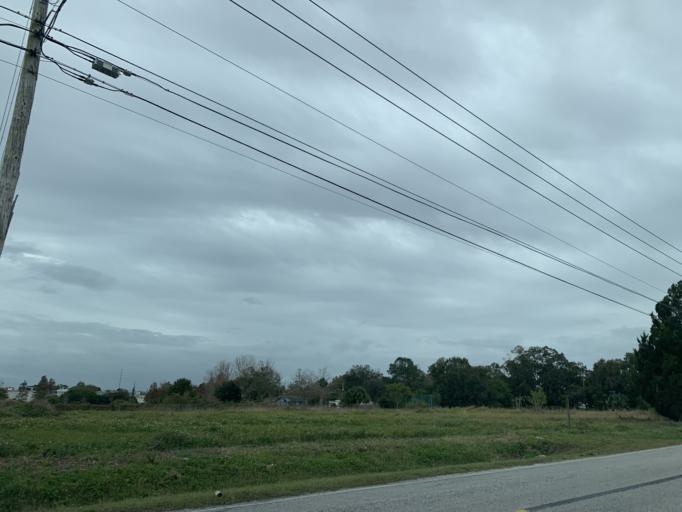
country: US
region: Florida
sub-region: Pinellas County
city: Belleair
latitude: 27.9367
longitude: -82.7916
